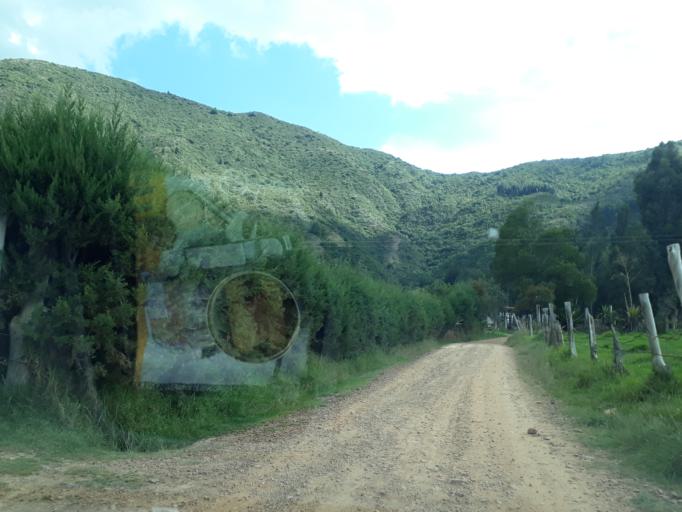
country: CO
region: Boyaca
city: Santa Rosa de Viterbo
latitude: 5.8500
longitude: -72.9567
